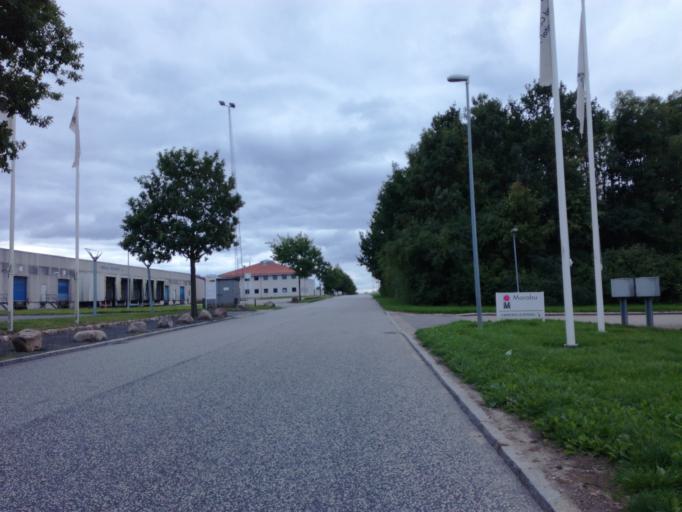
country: DK
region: South Denmark
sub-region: Vejle Kommune
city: Vejle
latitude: 55.6791
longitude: 9.5870
